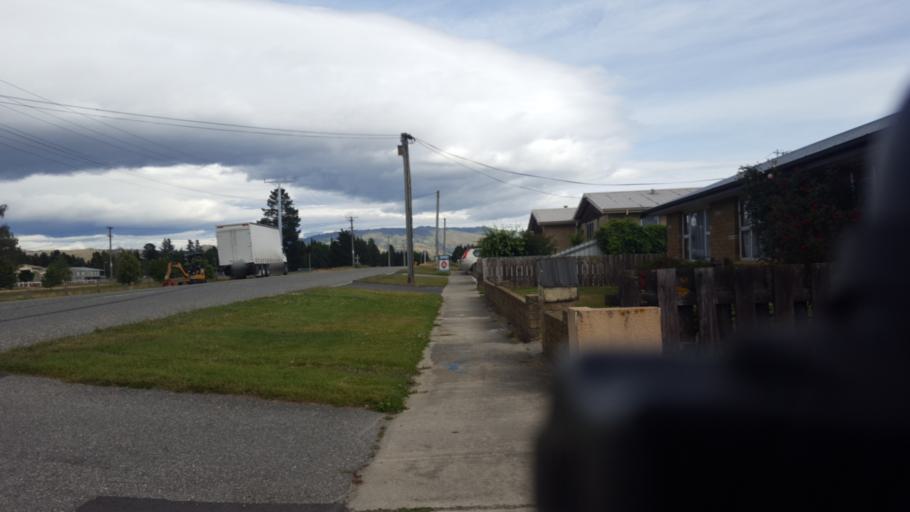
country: NZ
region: Otago
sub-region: Queenstown-Lakes District
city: Wanaka
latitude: -45.2415
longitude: 169.3909
